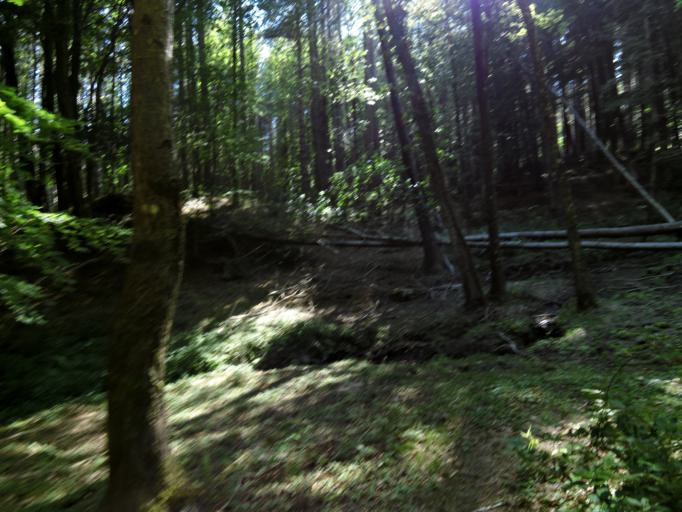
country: IT
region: Calabria
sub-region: Provincia di Vibo-Valentia
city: Nardodipace
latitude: 38.4965
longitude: 16.3849
